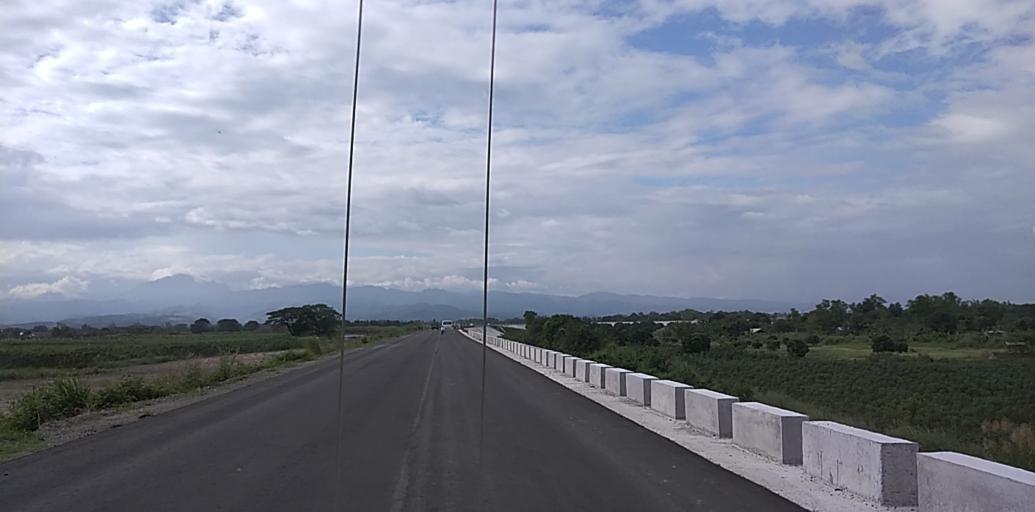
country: PH
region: Central Luzon
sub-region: Province of Pampanga
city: Pulung Santol
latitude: 15.0599
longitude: 120.5658
